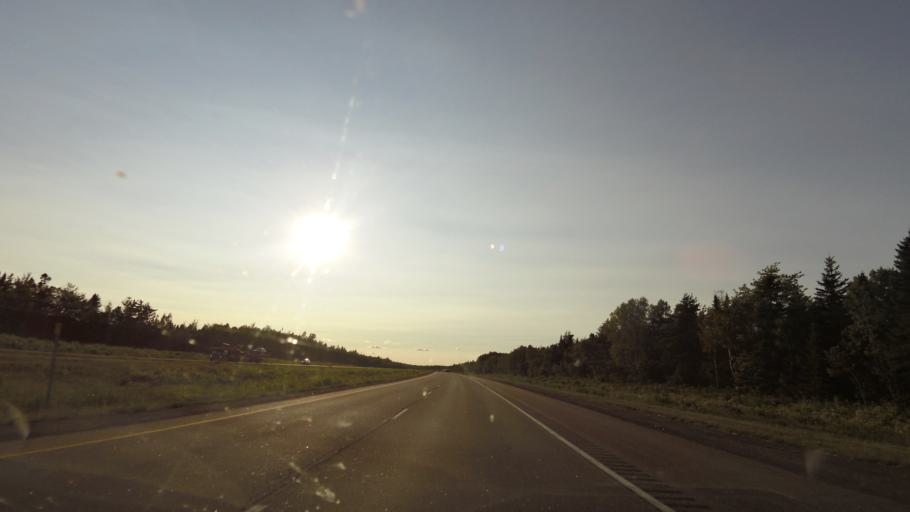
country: CA
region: New Brunswick
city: Dieppe
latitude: 46.1287
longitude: -64.6485
